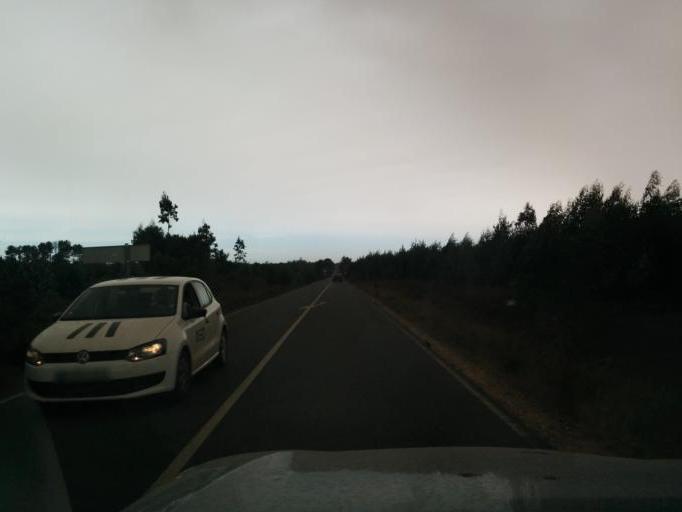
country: PT
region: Beja
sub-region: Odemira
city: Sao Teotonio
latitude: 37.5737
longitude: -8.7375
